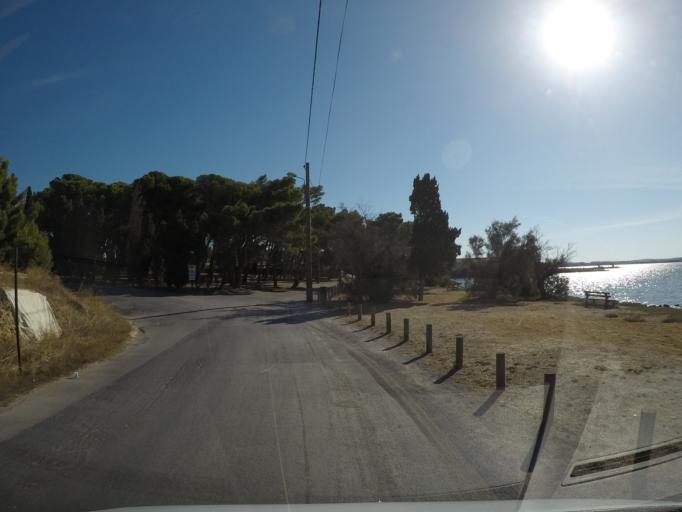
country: FR
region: Languedoc-Roussillon
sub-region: Departement de l'Aude
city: Narbonne
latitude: 43.1431
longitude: 3.0027
